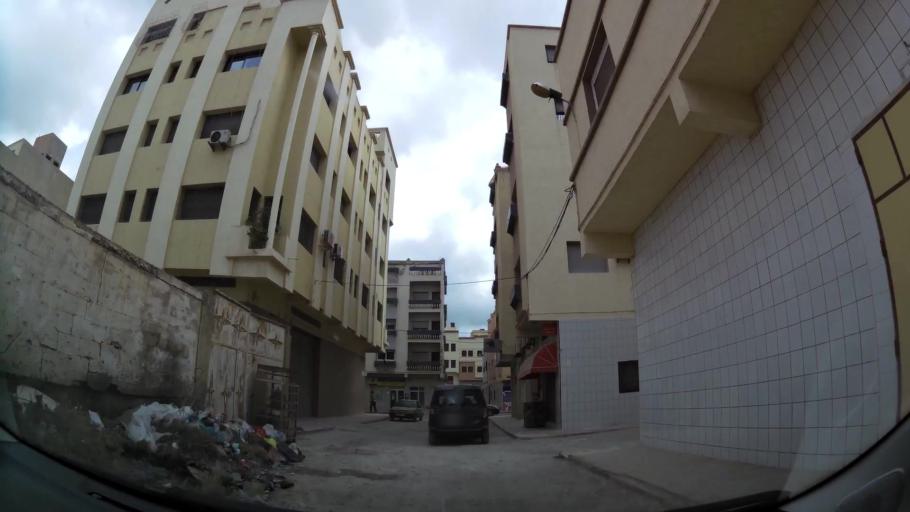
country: MA
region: Oriental
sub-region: Nador
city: Nador
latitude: 35.1684
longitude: -2.9357
